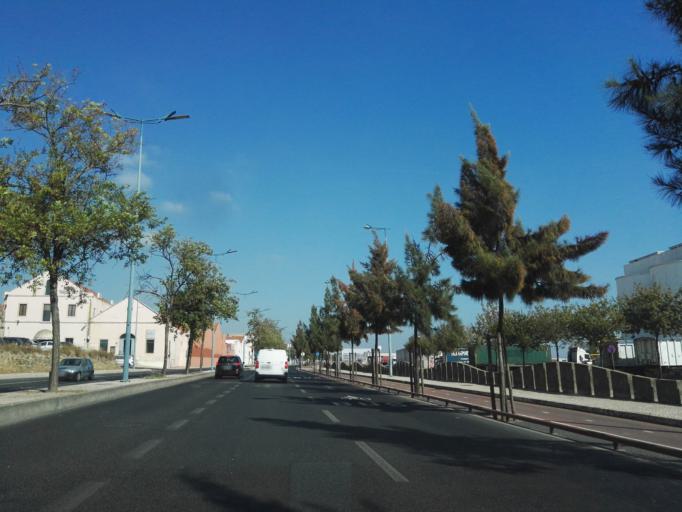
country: PT
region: Lisbon
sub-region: Lisbon
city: Lisbon
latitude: 38.7370
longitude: -9.1032
